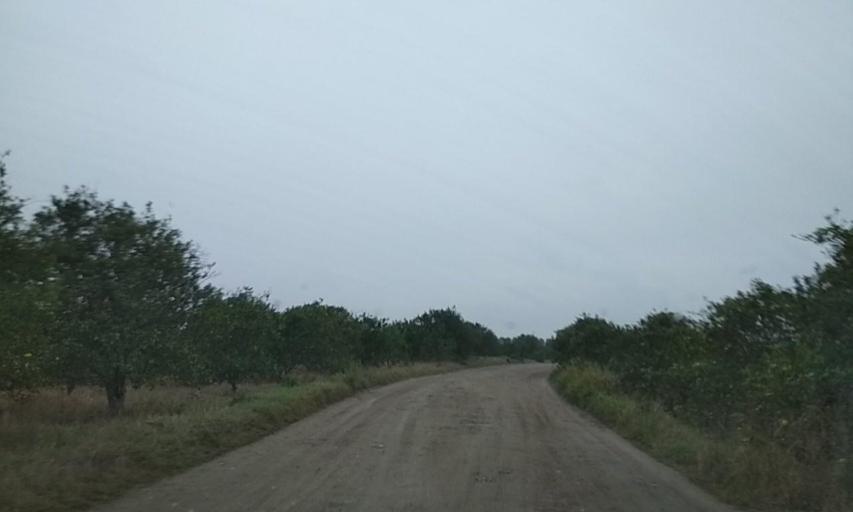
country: MX
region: Veracruz
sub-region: Papantla
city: El Chote
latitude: 20.3396
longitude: -97.3905
